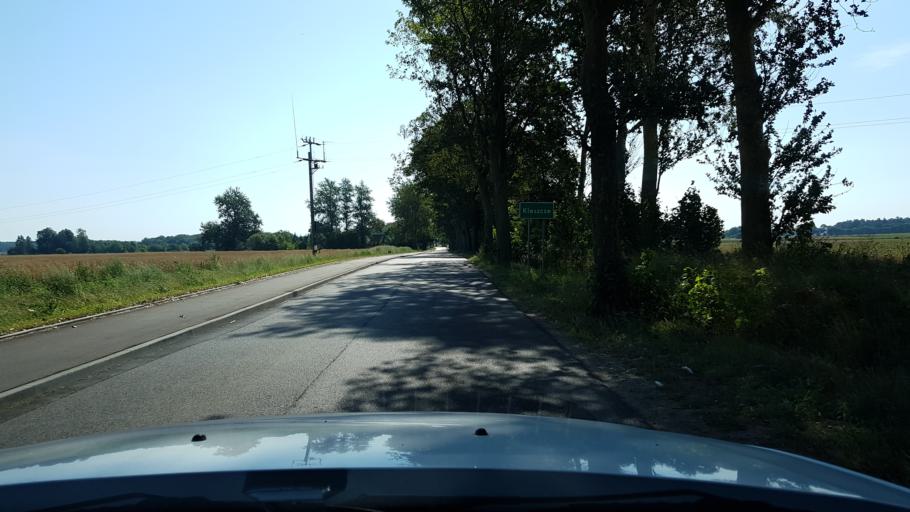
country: PL
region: West Pomeranian Voivodeship
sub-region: Powiat koszalinski
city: Sianow
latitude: 54.2748
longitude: 16.2271
